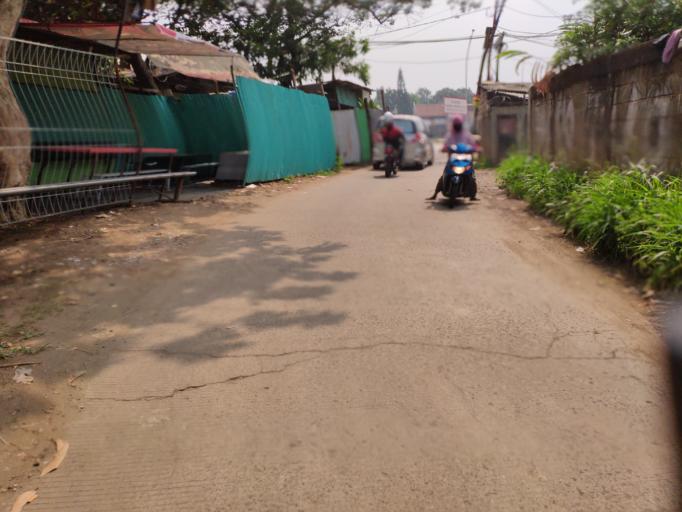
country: ID
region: West Java
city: Pamulang
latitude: -6.3217
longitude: 106.8027
